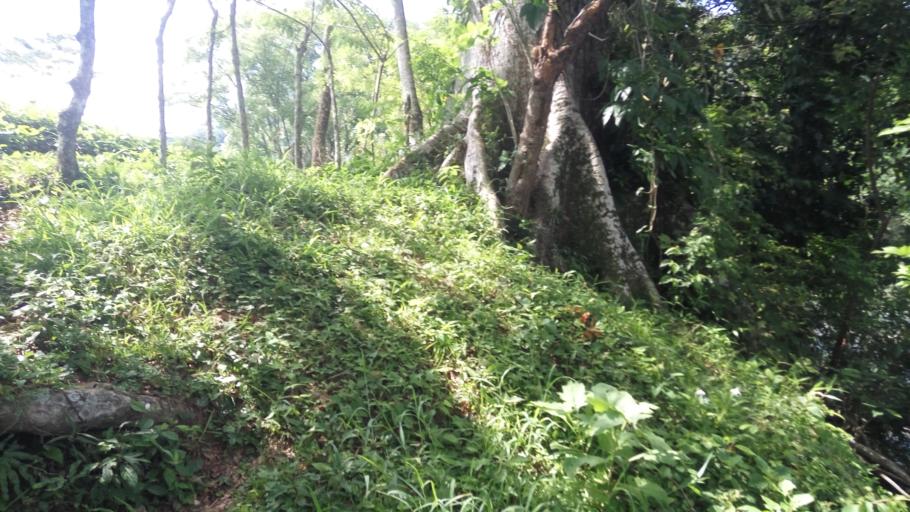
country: MX
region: Tabasco
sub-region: Teapa
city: Eureka y Belen
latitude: 17.5555
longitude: -92.9231
